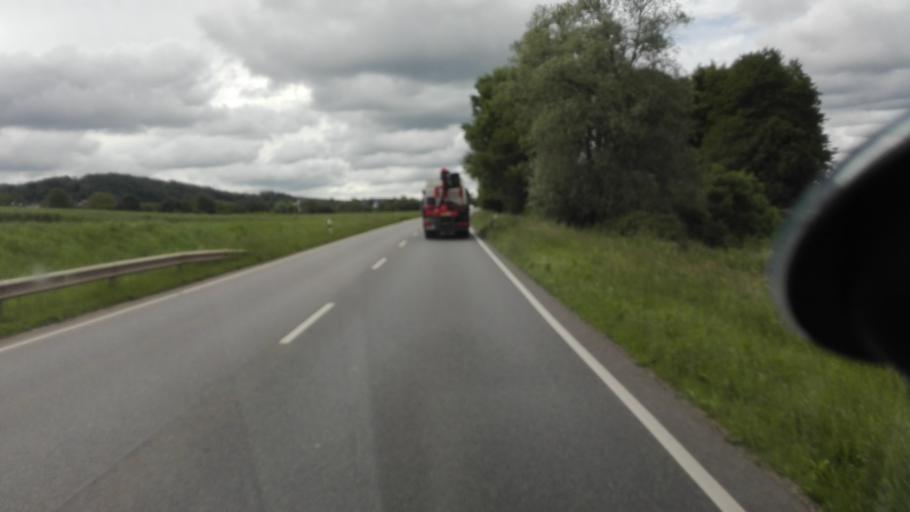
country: DE
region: Baden-Wuerttemberg
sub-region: Karlsruhe Region
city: Malsch
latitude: 49.2657
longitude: 8.6676
